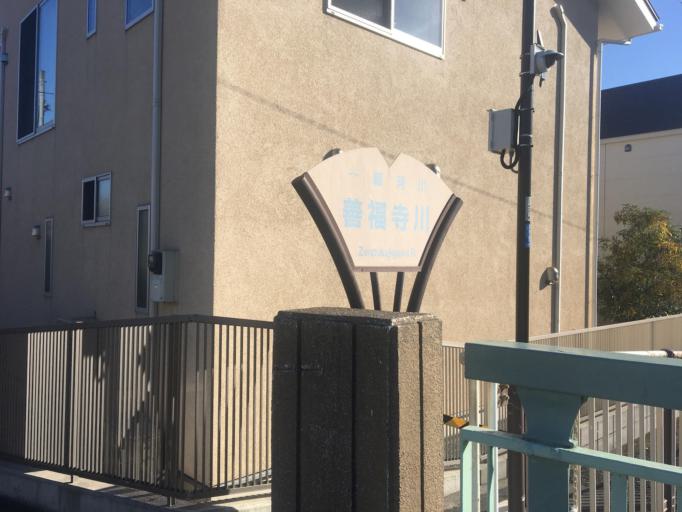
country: JP
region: Tokyo
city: Musashino
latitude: 35.7122
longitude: 139.5966
